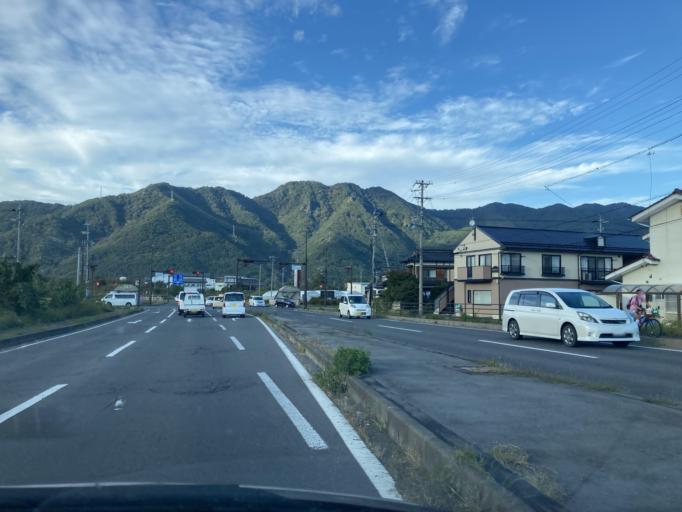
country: JP
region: Nagano
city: Ueda
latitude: 36.4027
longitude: 138.2097
